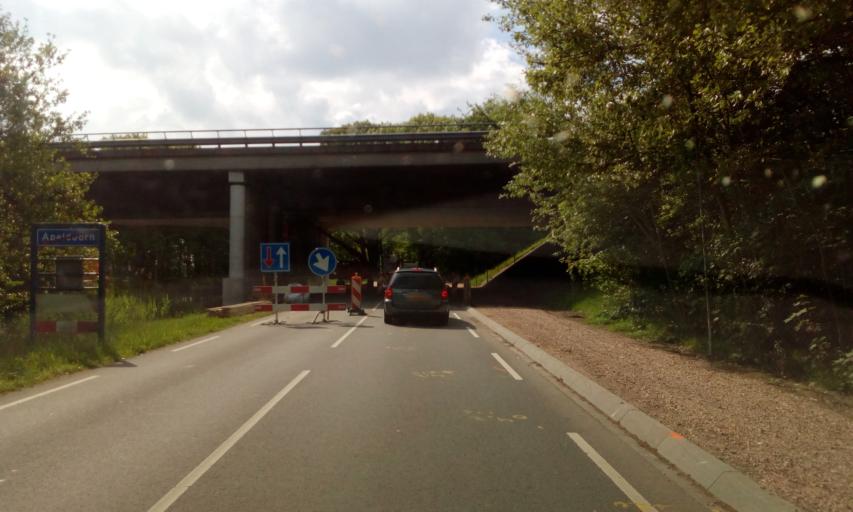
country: NL
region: Gelderland
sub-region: Gemeente Apeldoorn
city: Beekbergen
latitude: 52.1806
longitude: 5.9910
